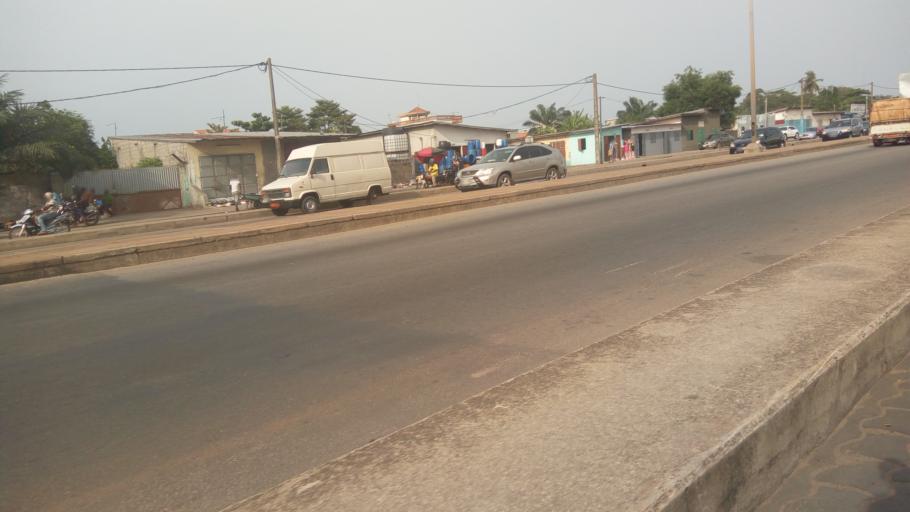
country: BJ
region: Littoral
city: Cotonou
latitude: 6.3871
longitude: 2.3691
